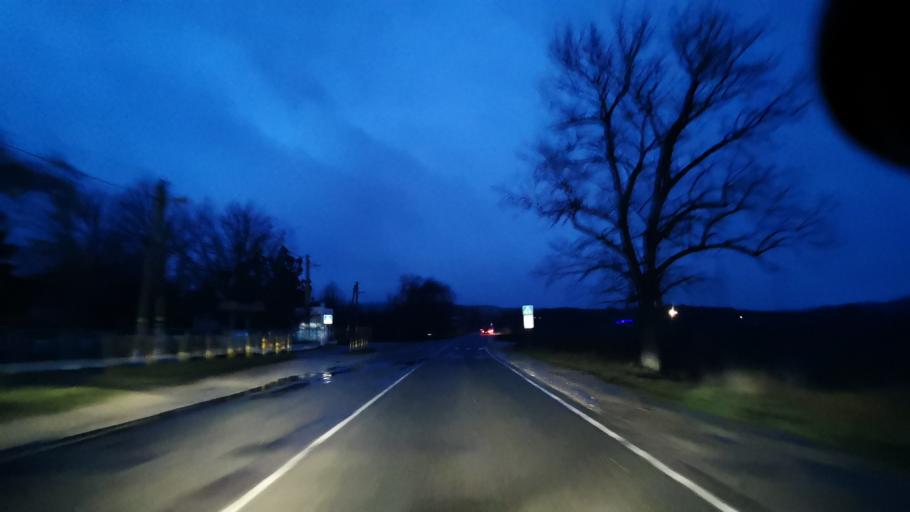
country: MD
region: Orhei
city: Orhei
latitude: 47.4559
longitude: 28.7912
